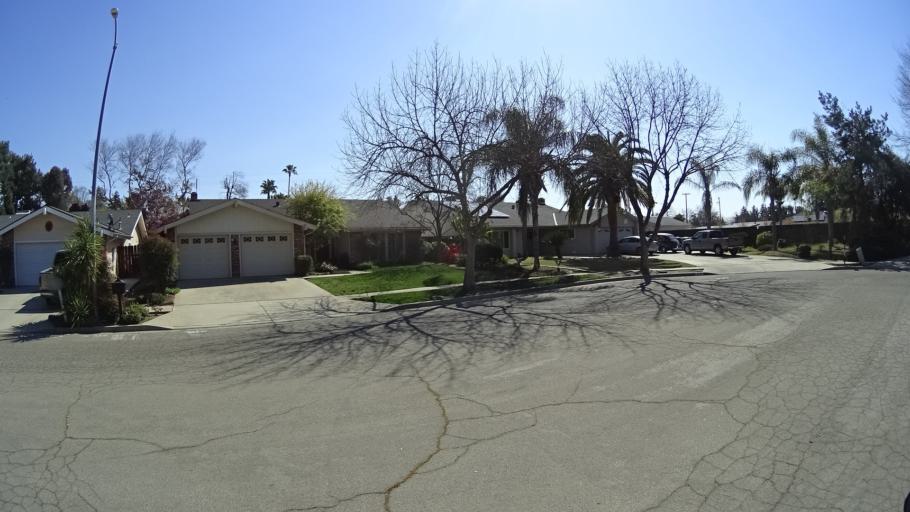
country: US
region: California
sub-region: Fresno County
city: Clovis
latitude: 36.8314
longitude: -119.7344
